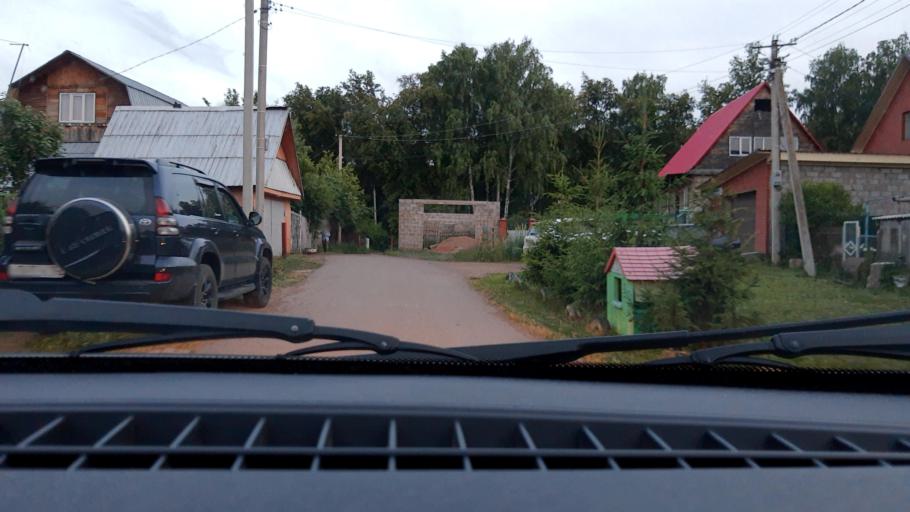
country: RU
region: Bashkortostan
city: Mikhaylovka
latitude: 54.8009
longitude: 55.7715
